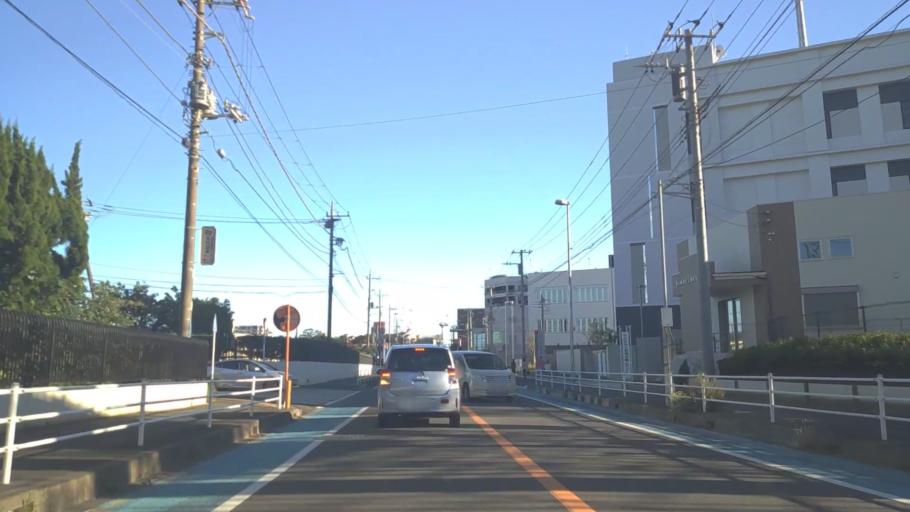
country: JP
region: Kanagawa
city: Chigasaki
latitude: 35.3381
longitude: 139.4025
